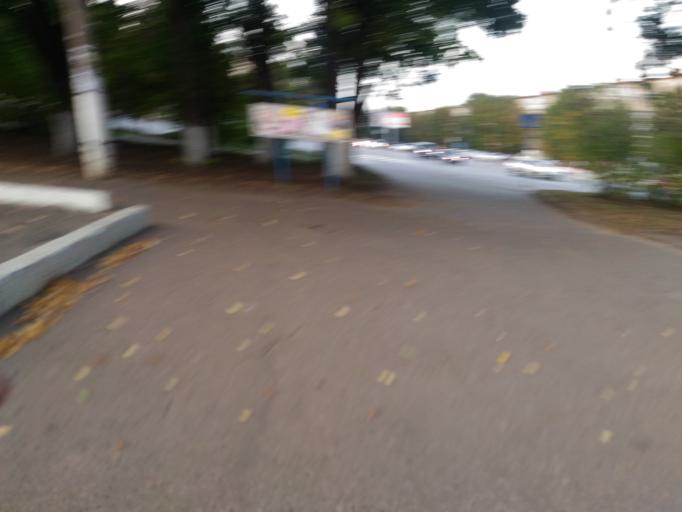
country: RU
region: Ulyanovsk
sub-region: Ulyanovskiy Rayon
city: Ulyanovsk
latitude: 54.3031
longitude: 48.3303
